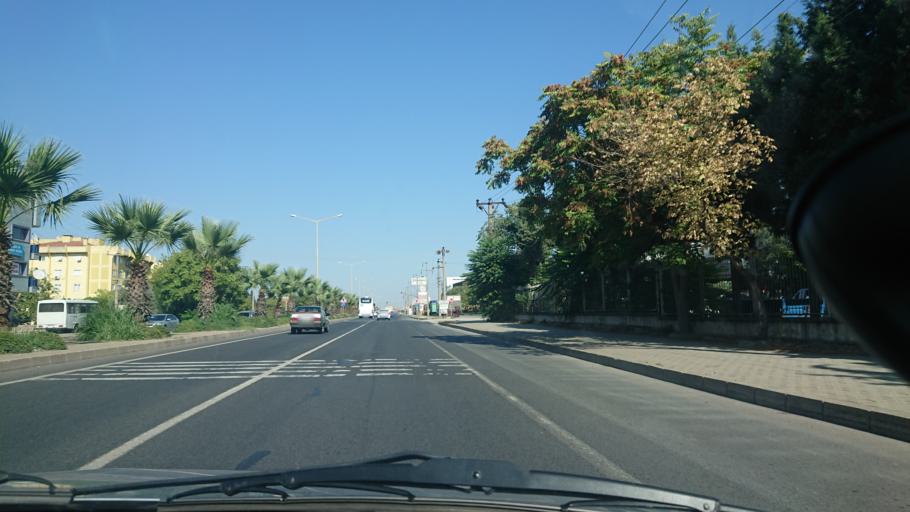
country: TR
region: Manisa
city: Turgutlu
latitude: 38.4940
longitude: 27.7180
